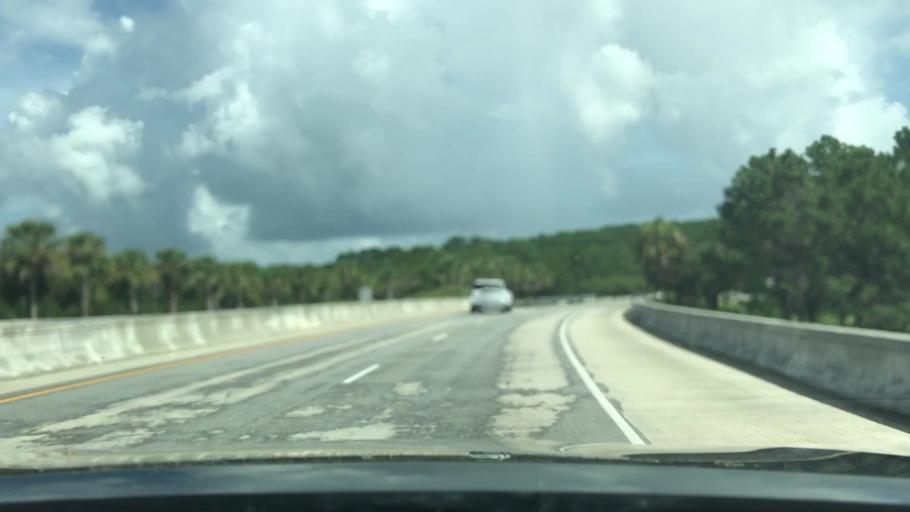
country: US
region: South Carolina
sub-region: Beaufort County
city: Hilton Head Island
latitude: 32.2146
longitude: -80.7388
